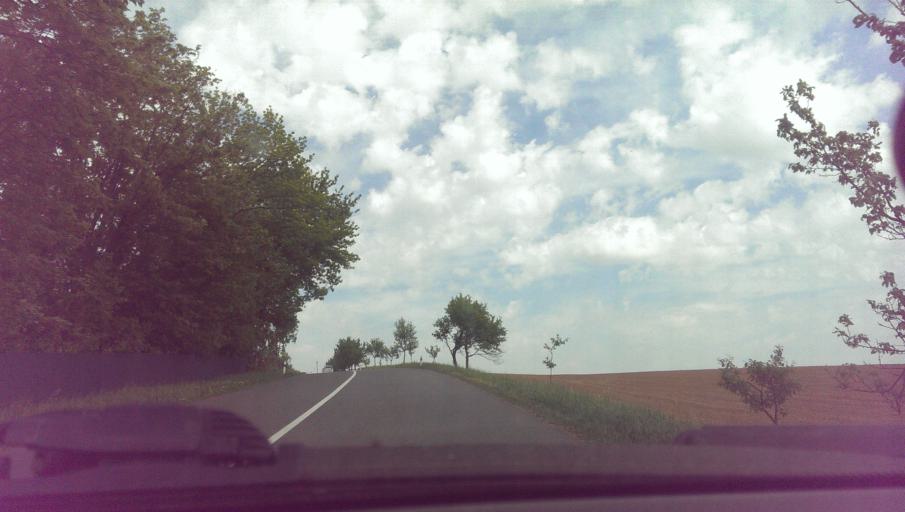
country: CZ
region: Zlin
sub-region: Okres Zlin
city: Otrokovice
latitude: 49.2488
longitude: 17.5435
